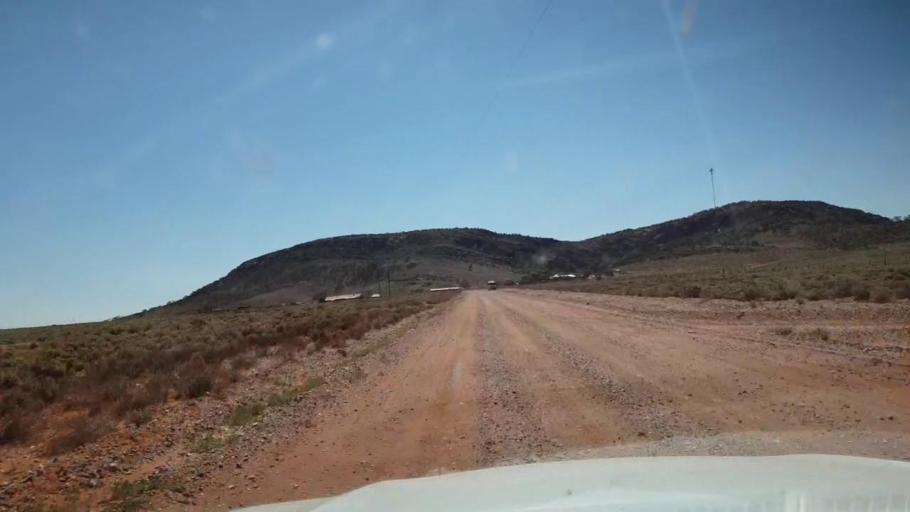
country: AU
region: South Australia
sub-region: Whyalla
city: Whyalla
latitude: -32.6899
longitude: 137.1280
